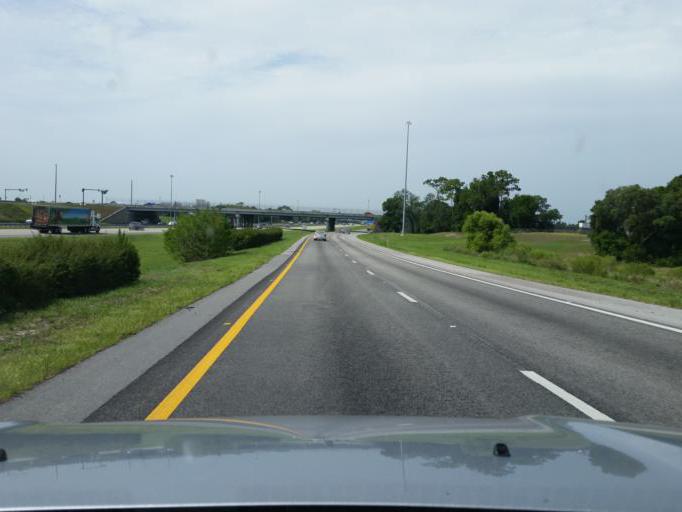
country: US
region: Florida
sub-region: Seminole County
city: Heathrow
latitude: 28.7893
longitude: -81.3499
